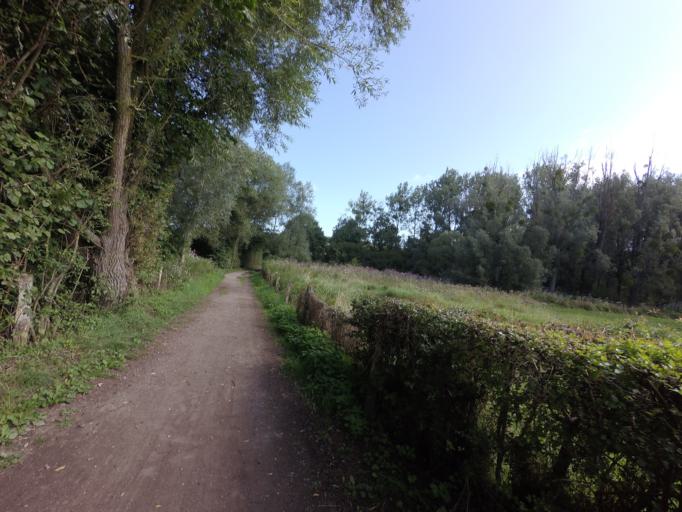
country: BE
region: Wallonia
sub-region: Province de Liege
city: Plombieres
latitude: 50.7582
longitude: 5.9350
